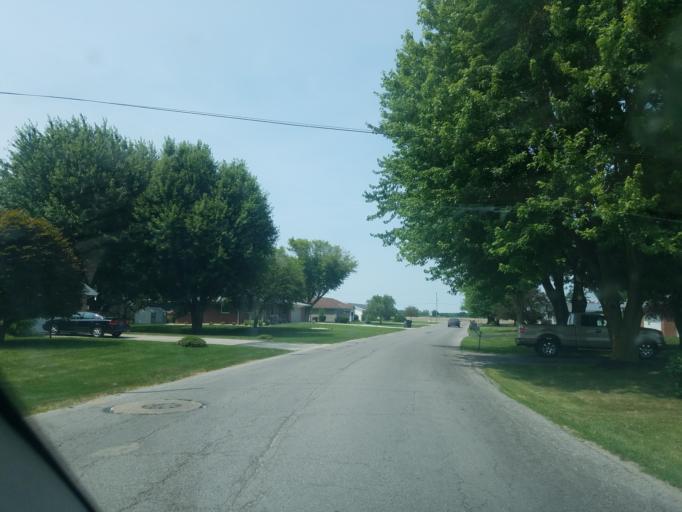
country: US
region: Ohio
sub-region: Seneca County
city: Tiffin
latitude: 41.1147
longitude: -83.2072
